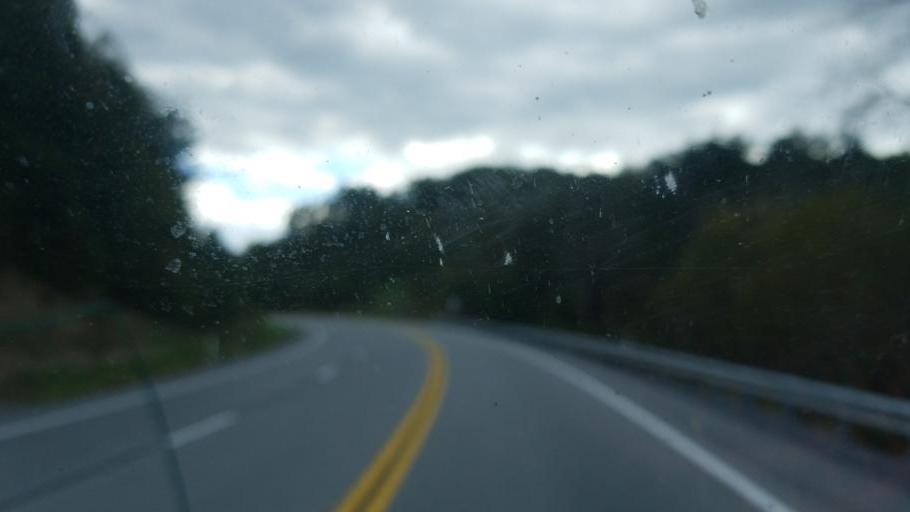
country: US
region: Pennsylvania
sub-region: Fulton County
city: McConnellsburg
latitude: 39.9382
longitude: -78.0196
